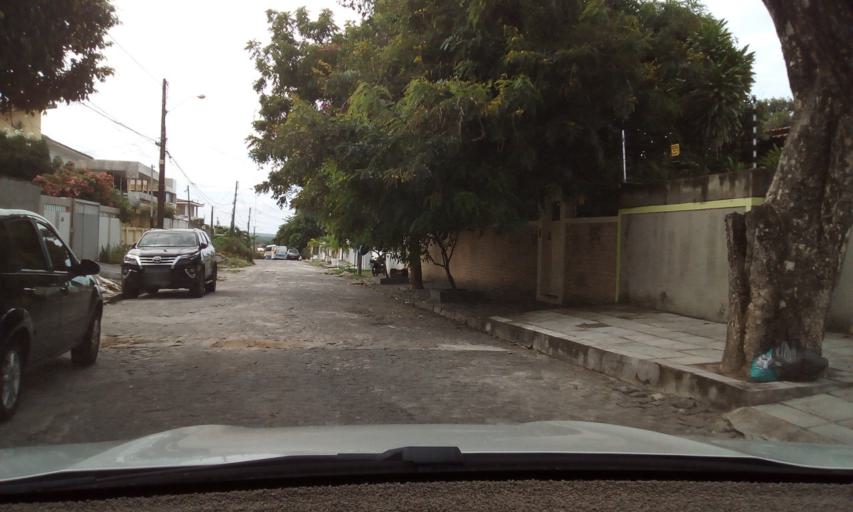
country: BR
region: Paraiba
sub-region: Joao Pessoa
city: Joao Pessoa
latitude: -7.1076
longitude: -34.8529
